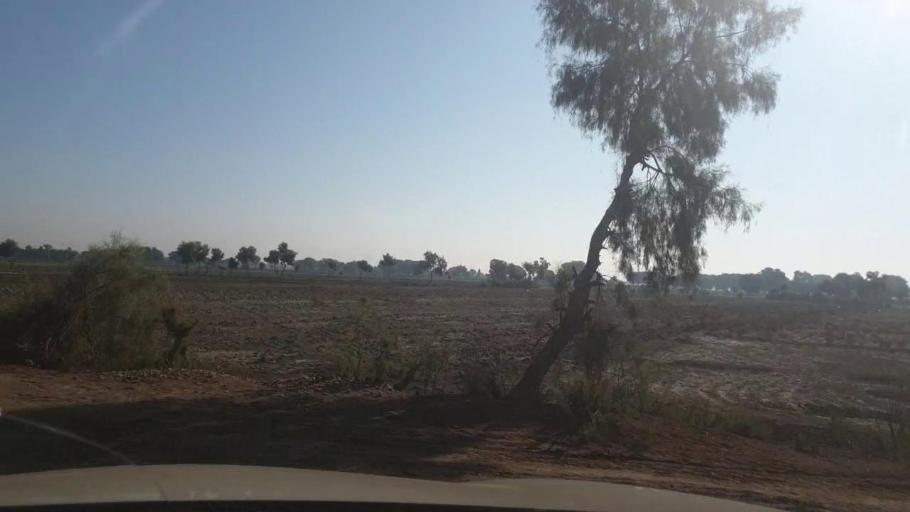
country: PK
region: Sindh
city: Bhan
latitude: 26.5358
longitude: 67.6891
